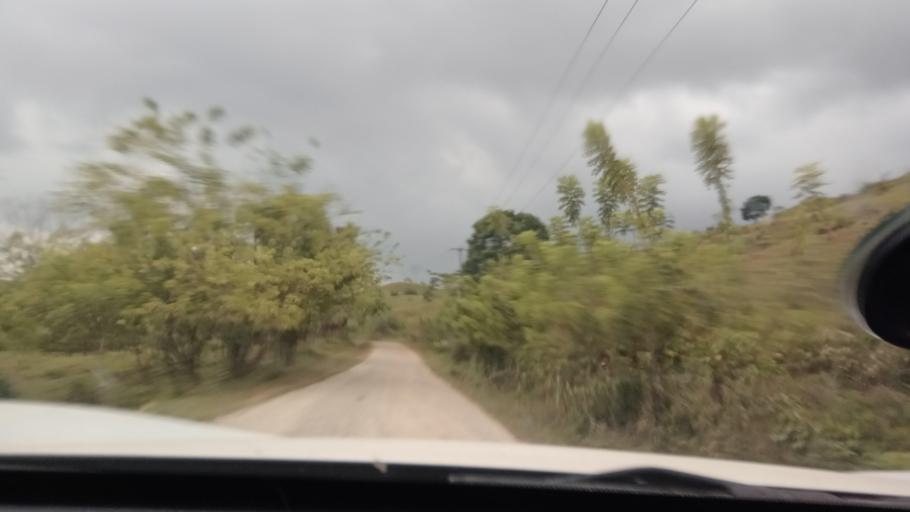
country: MX
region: Tabasco
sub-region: Huimanguillo
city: Francisco Rueda
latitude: 17.4372
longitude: -94.0568
